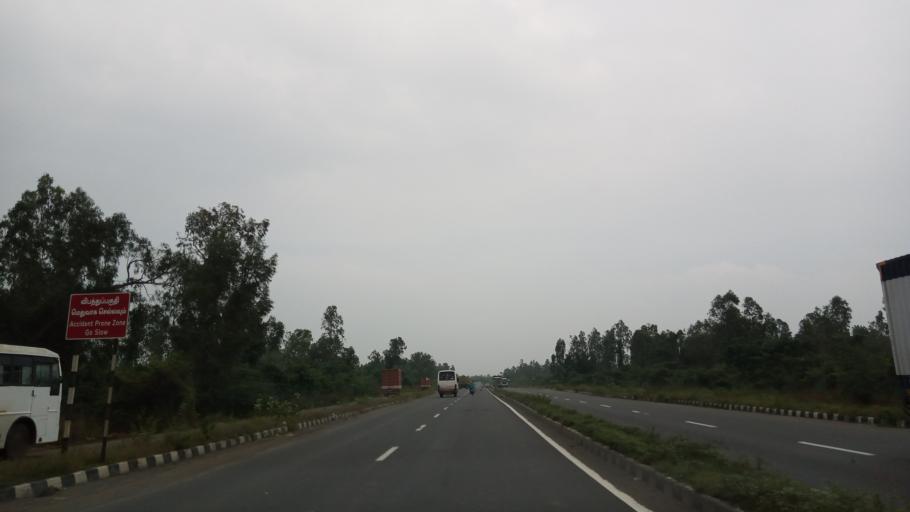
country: IN
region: Tamil Nadu
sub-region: Kancheepuram
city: Madambakkam
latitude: 12.8560
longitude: 79.9522
